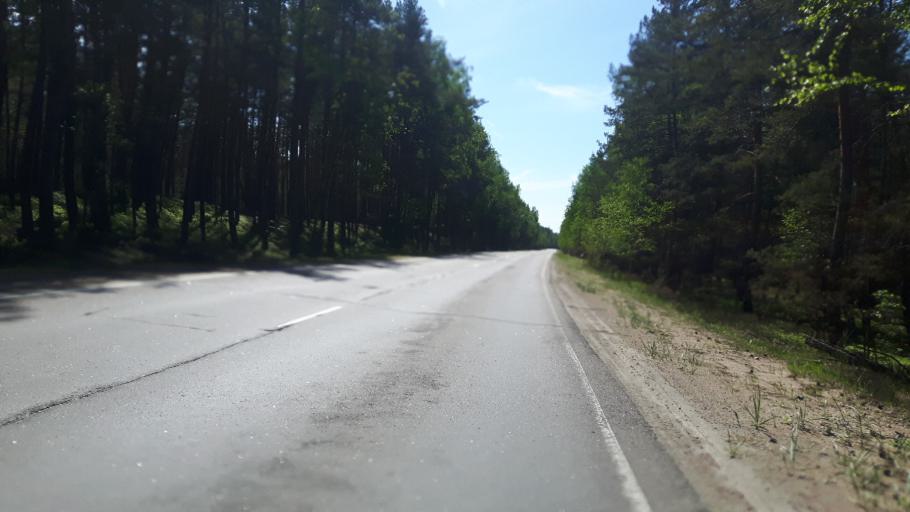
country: RU
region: Leningrad
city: Sista-Palkino
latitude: 59.7740
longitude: 28.8526
